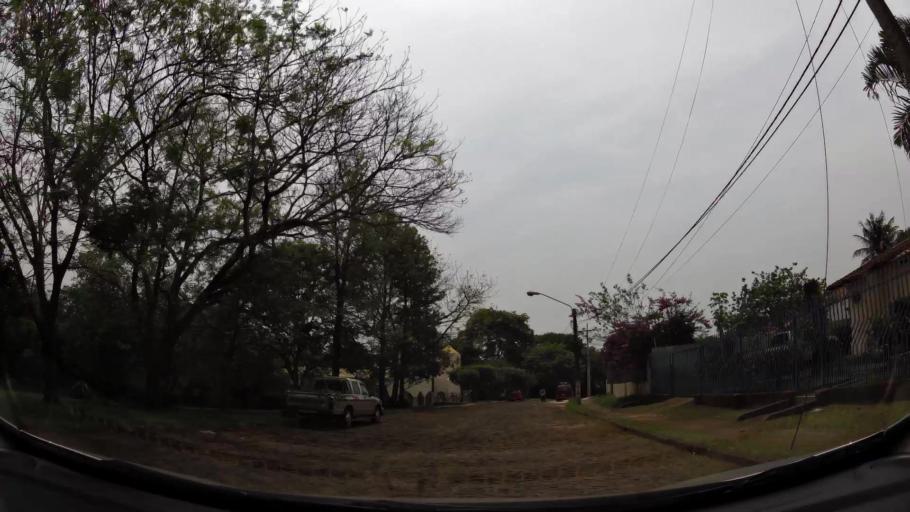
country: PY
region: Alto Parana
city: Presidente Franco
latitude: -25.5510
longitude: -54.6199
